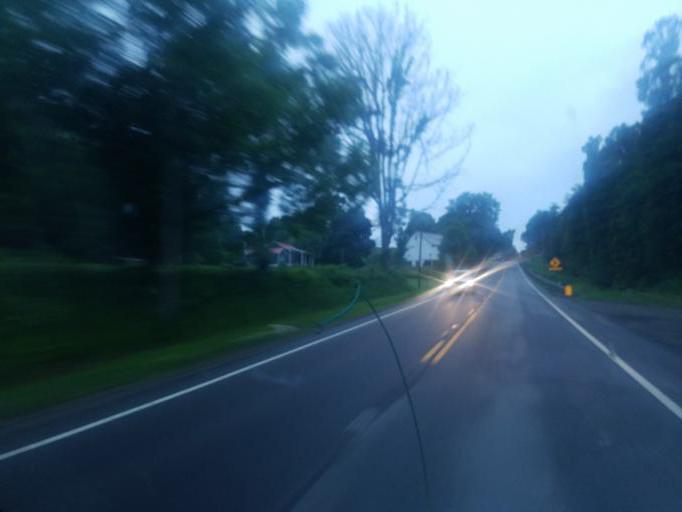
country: US
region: Ohio
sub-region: Carroll County
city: Carrollton
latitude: 40.5437
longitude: -81.0346
